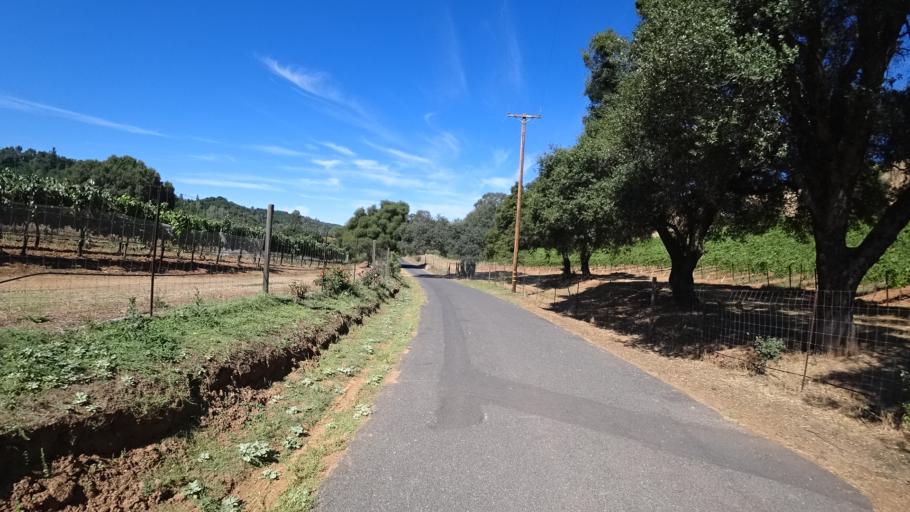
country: US
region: California
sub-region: Calaveras County
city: Mountain Ranch
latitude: 38.1509
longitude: -120.5500
